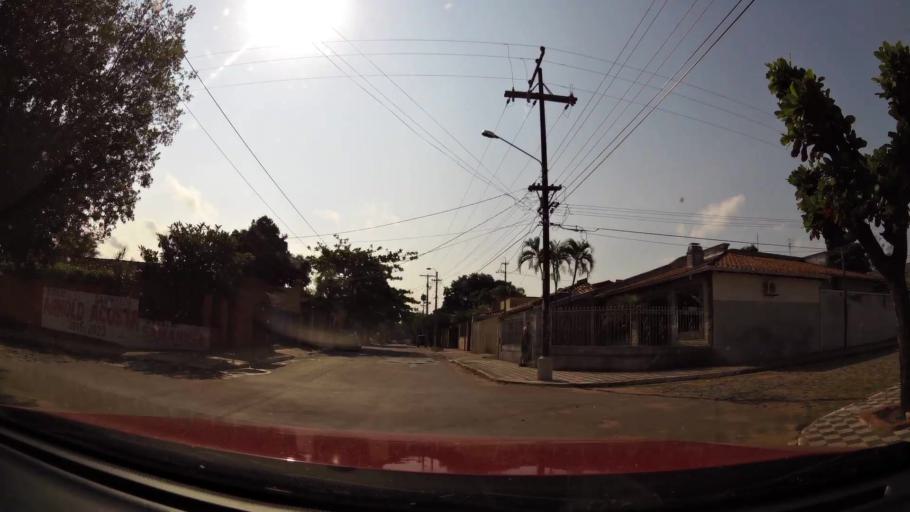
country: PY
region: Asuncion
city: Asuncion
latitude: -25.3157
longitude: -57.6404
